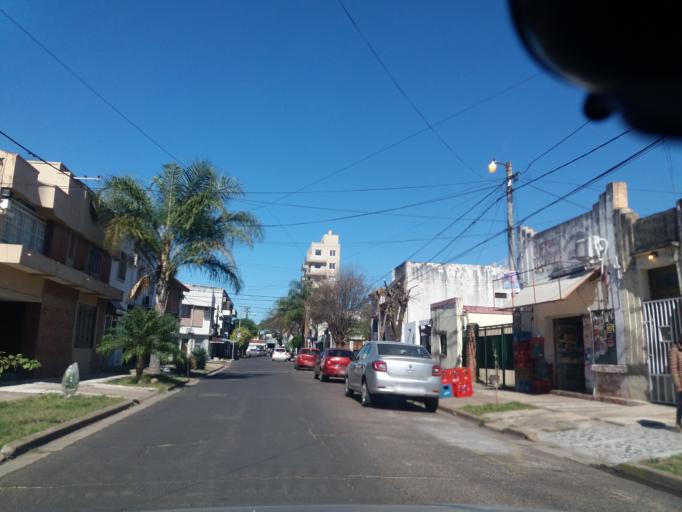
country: AR
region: Corrientes
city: Corrientes
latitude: -27.4732
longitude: -58.8447
